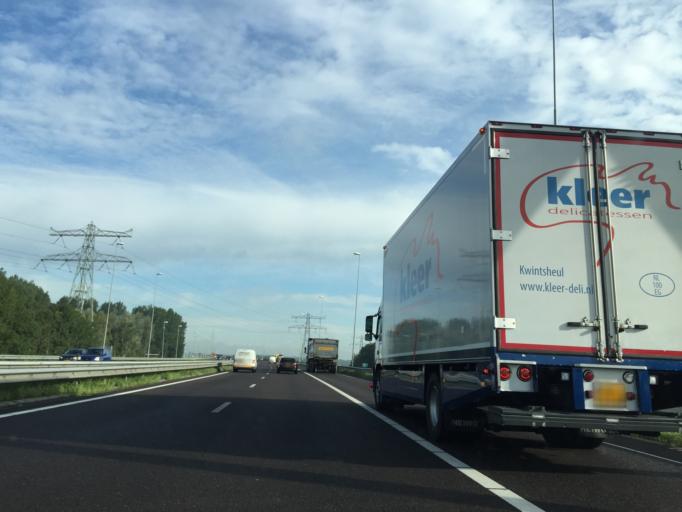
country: NL
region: North Holland
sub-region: Gemeente Haarlem
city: Haarlem
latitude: 52.4019
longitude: 4.7048
